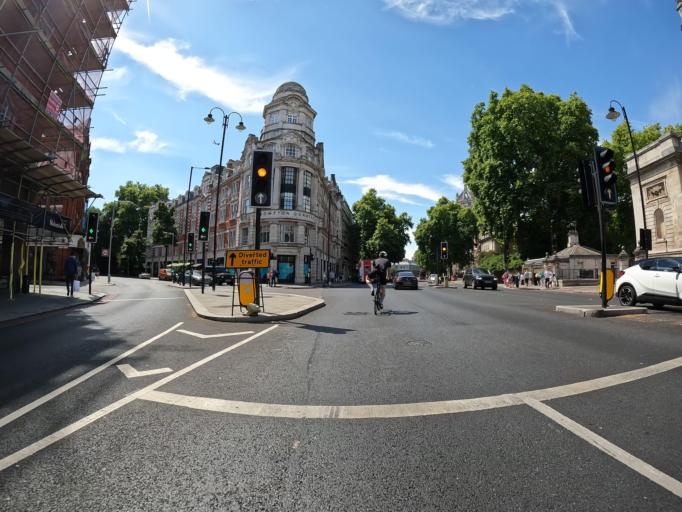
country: GB
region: England
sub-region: Greater London
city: Chelsea
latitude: 51.4963
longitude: -0.1688
